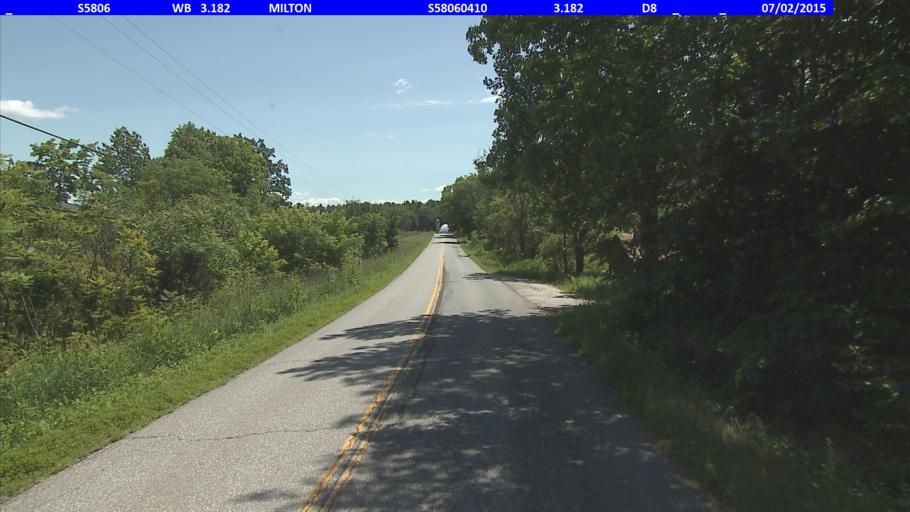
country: US
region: Vermont
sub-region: Chittenden County
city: Milton
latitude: 44.6697
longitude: -73.1702
